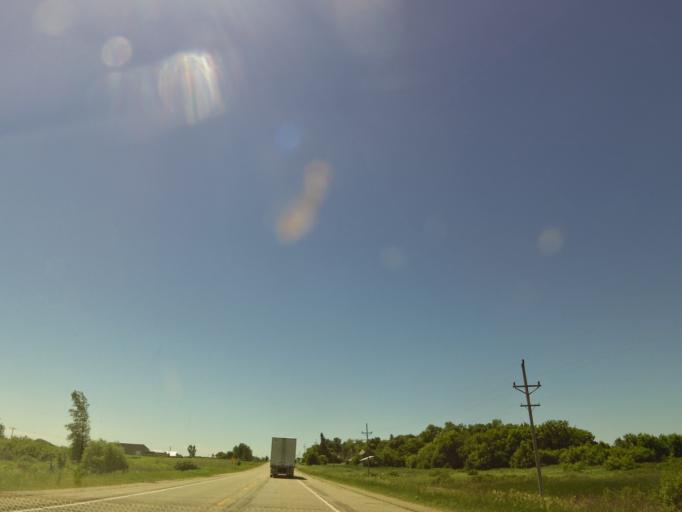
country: US
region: Minnesota
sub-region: Mahnomen County
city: Mahnomen
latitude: 47.1737
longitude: -95.9334
